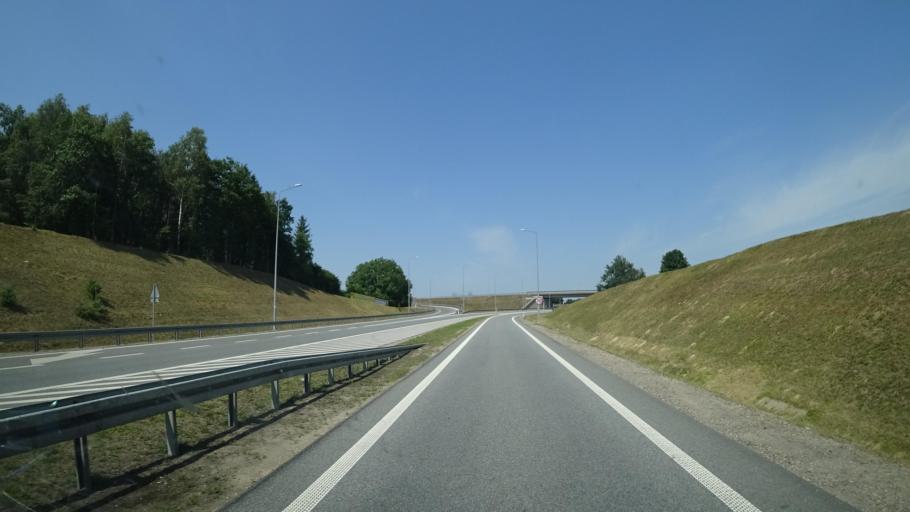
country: PL
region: Pomeranian Voivodeship
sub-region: Powiat koscierski
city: Koscierzyna
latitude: 54.1344
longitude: 18.0138
